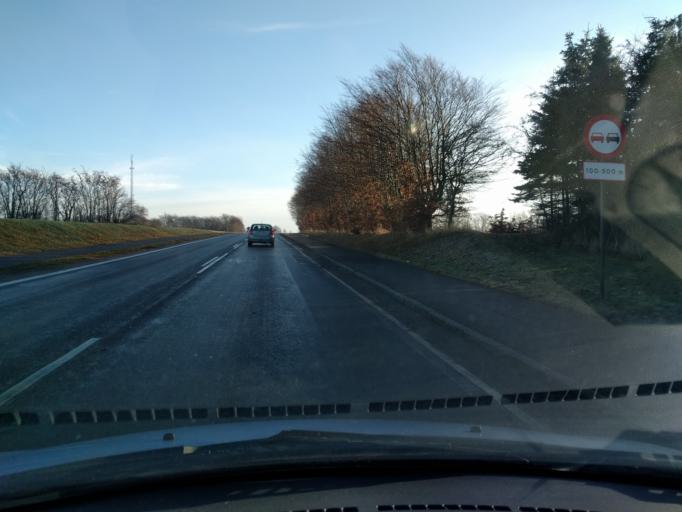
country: DK
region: South Denmark
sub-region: Odense Kommune
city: Neder Holluf
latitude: 55.3905
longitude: 10.4597
